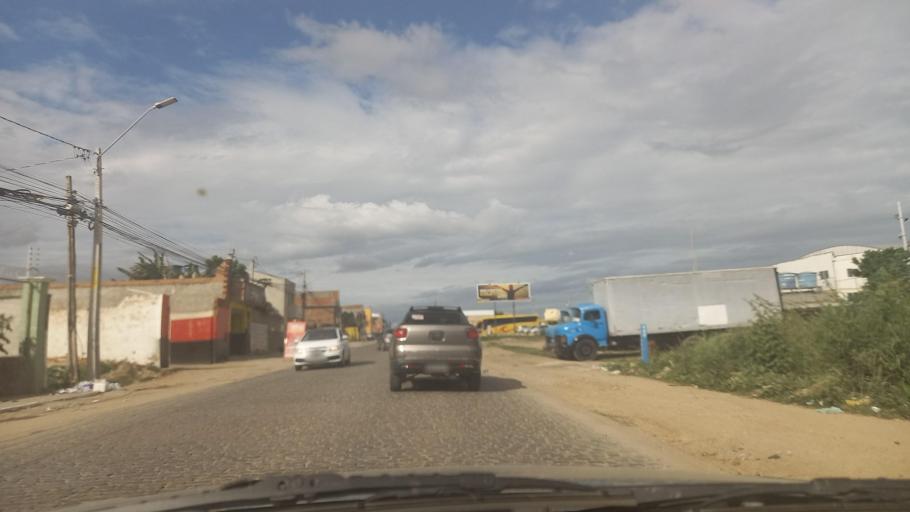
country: BR
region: Pernambuco
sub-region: Caruaru
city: Caruaru
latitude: -8.2883
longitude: -36.0087
